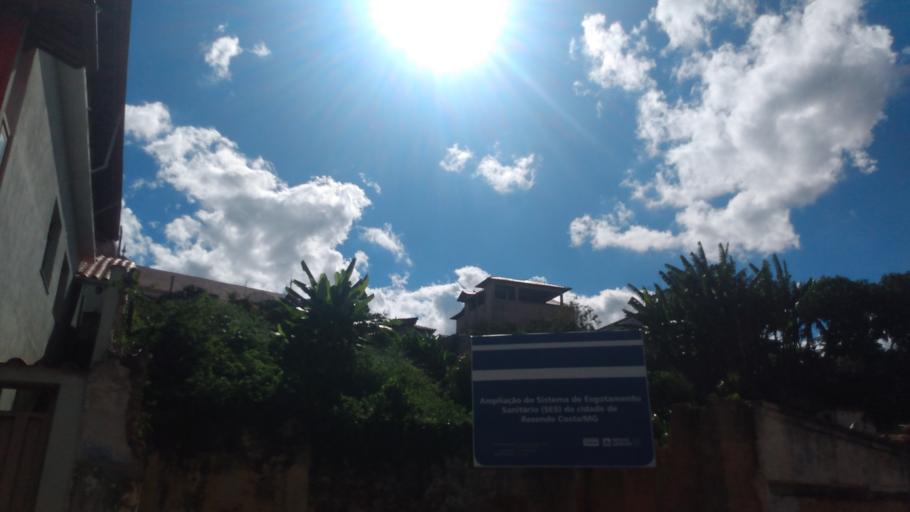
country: BR
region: Minas Gerais
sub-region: Tiradentes
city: Tiradentes
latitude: -20.9229
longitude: -44.2371
